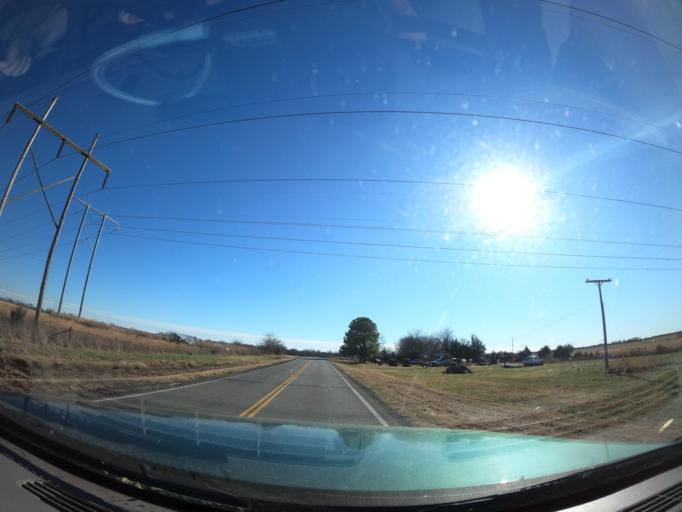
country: US
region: Oklahoma
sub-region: McIntosh County
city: Checotah
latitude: 35.5759
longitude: -95.6595
